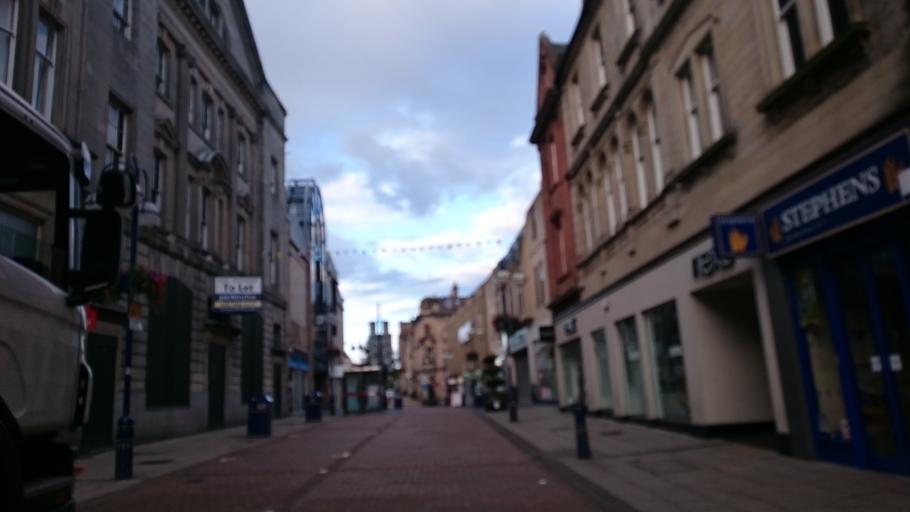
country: GB
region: Scotland
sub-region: Fife
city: Dunfermline
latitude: 56.0715
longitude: -3.4604
